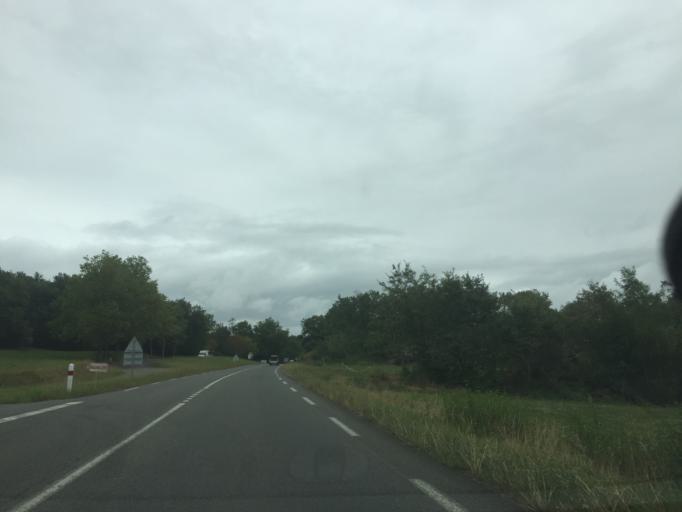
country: FR
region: Midi-Pyrenees
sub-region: Departement des Hautes-Pyrenees
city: Rabastens-de-Bigorre
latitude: 43.4123
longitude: 0.2199
